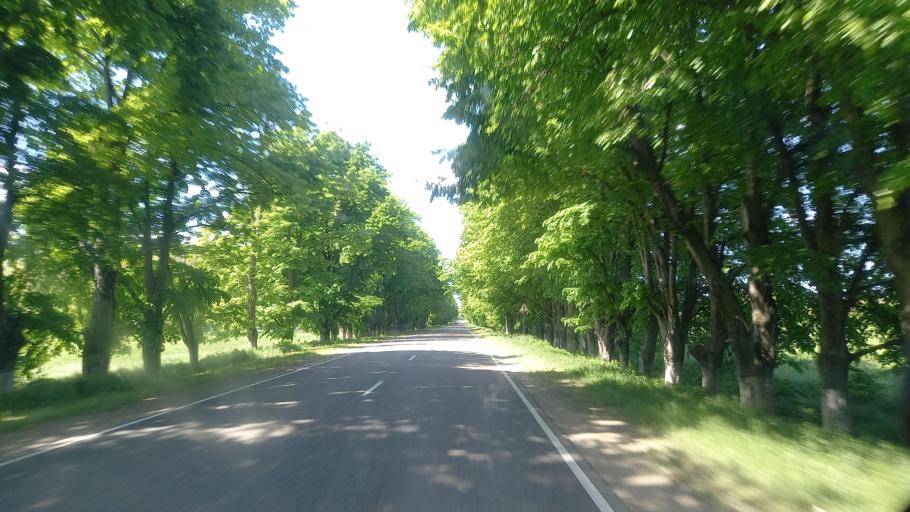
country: RU
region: Krasnodarskiy
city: Kazanskaya
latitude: 45.3751
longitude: 40.4644
